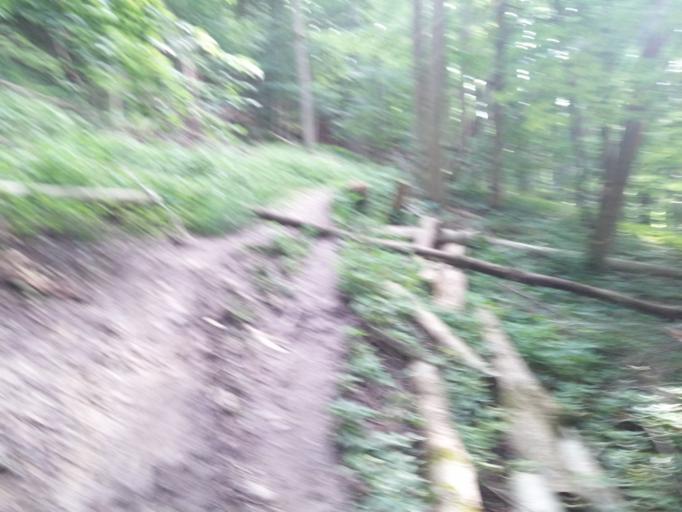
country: DE
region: Bavaria
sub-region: Swabia
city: Kronburg
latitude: 47.8636
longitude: 10.1883
